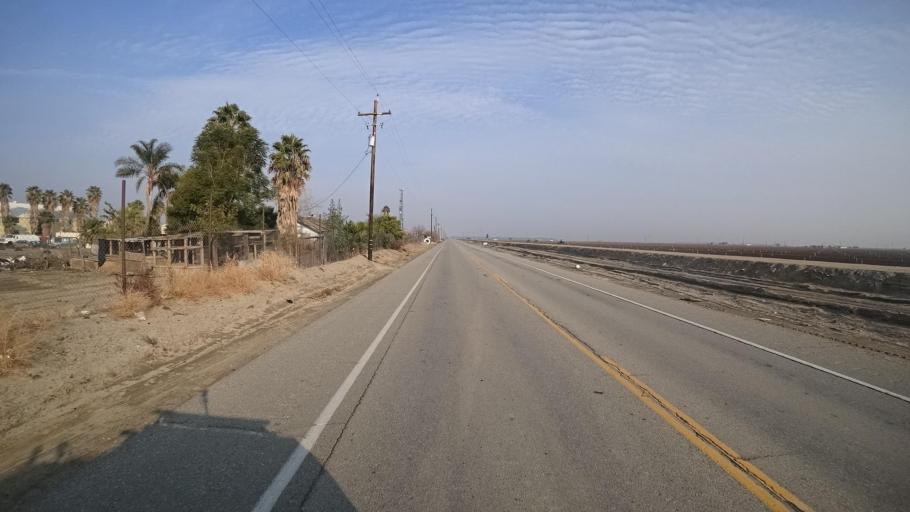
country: US
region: California
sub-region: Kern County
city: Weedpatch
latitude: 35.1099
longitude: -118.9147
